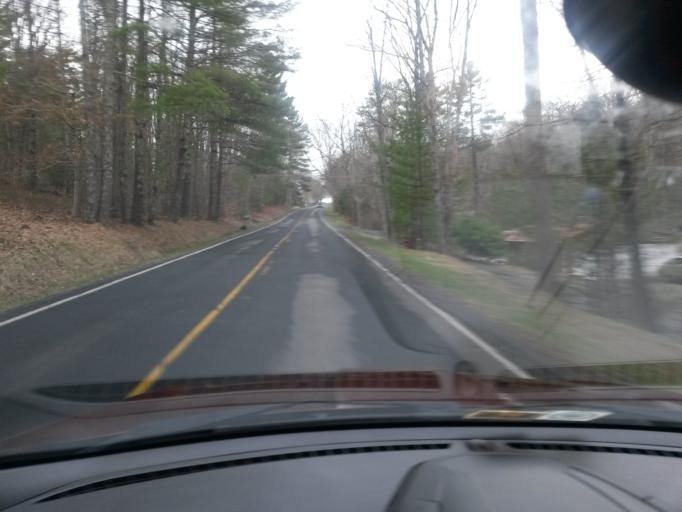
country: US
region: Virginia
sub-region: Bath County
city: Warm Springs
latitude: 38.0991
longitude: -79.7751
